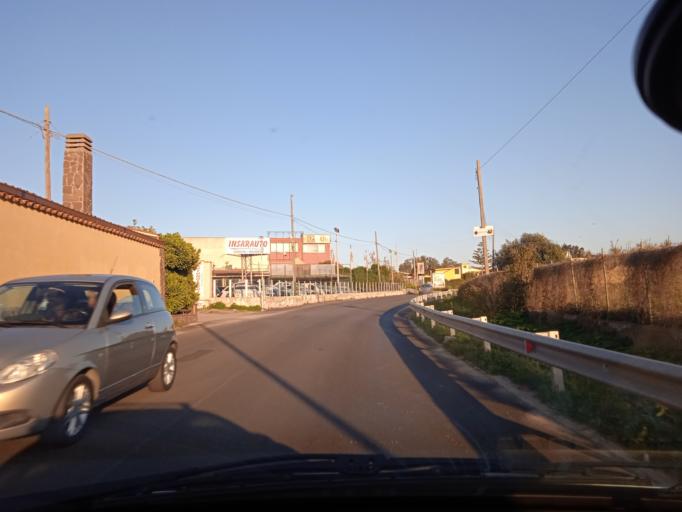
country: IT
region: Sicily
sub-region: Palermo
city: Ficarazzi
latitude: 38.0917
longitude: 13.4871
